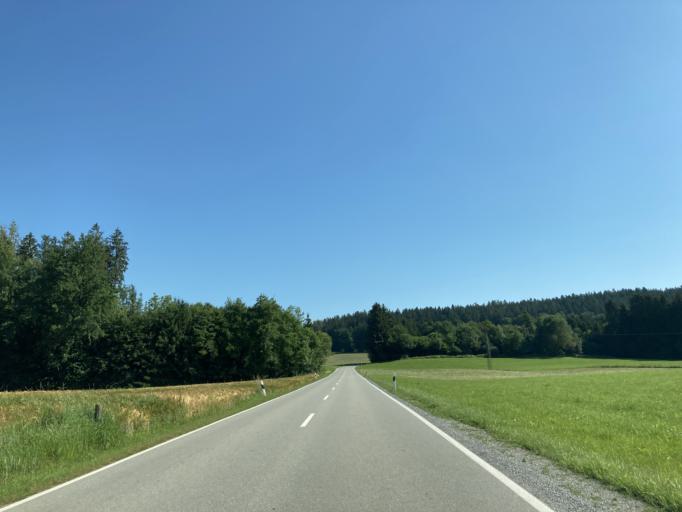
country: DE
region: Bavaria
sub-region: Upper Bavaria
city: Bad Endorf
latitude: 47.9327
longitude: 12.3011
